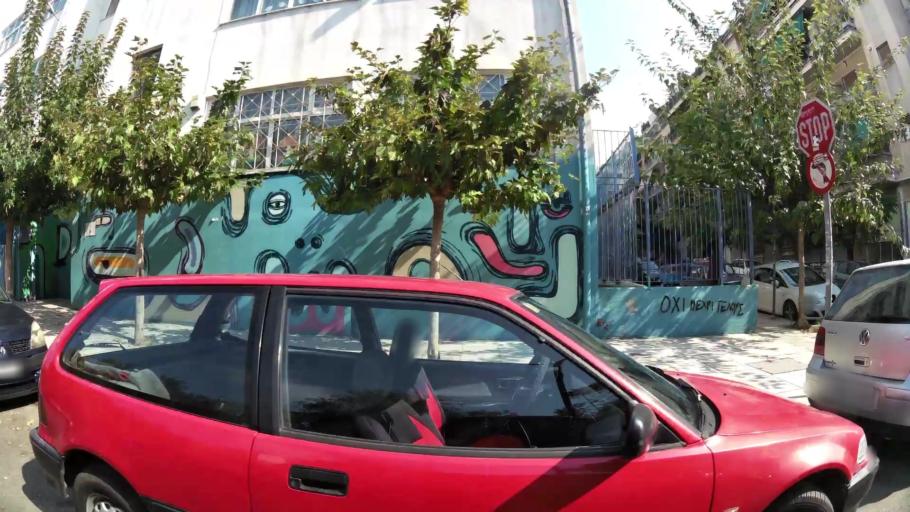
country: GR
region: Attica
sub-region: Nomarchia Athinas
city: Kipseli
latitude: 38.0095
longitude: 23.7324
